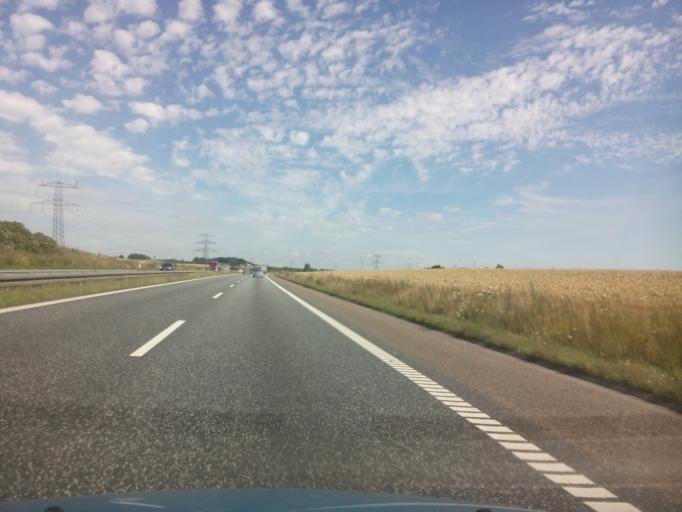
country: DK
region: Central Jutland
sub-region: Arhus Kommune
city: Trige
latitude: 56.2666
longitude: 10.1286
